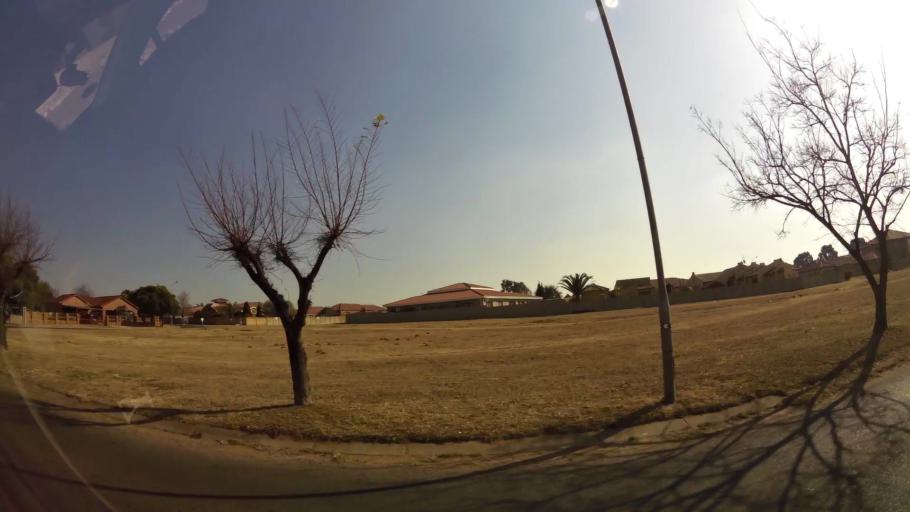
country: ZA
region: Gauteng
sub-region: West Rand District Municipality
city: Randfontein
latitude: -26.1811
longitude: 27.6804
